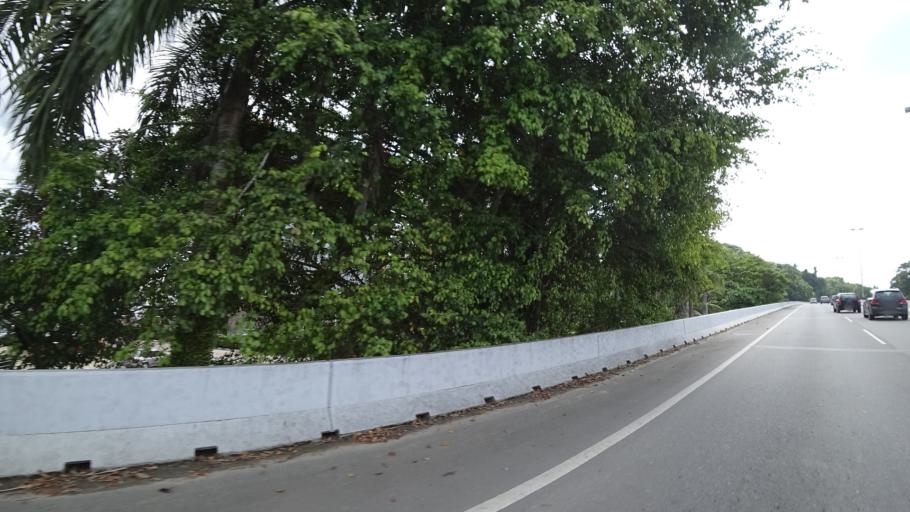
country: BN
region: Brunei and Muara
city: Bandar Seri Begawan
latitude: 4.8888
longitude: 114.9323
